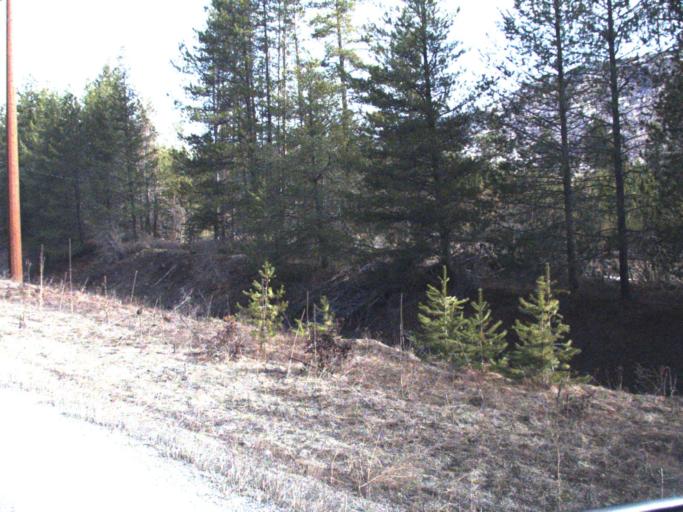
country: US
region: Washington
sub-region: Stevens County
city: Chewelah
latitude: 48.6421
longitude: -117.3740
